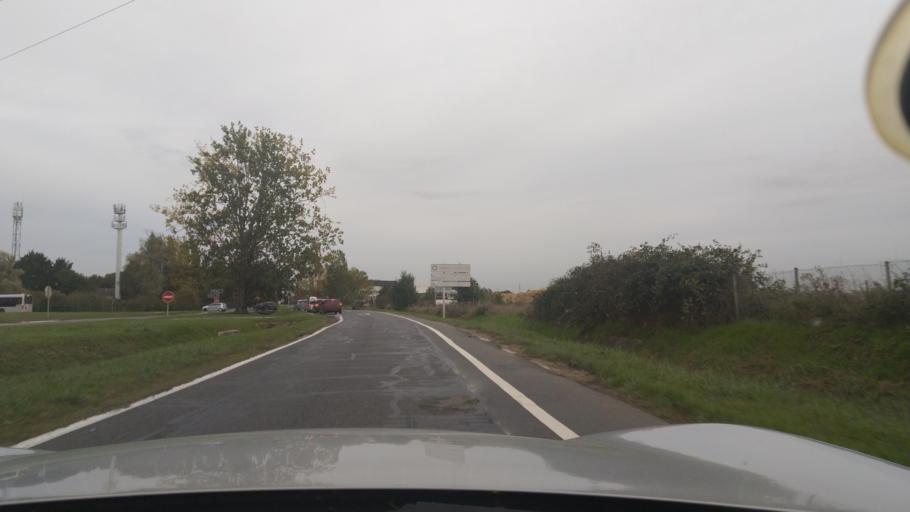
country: FR
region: Ile-de-France
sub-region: Departement de Seine-Saint-Denis
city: Villepinte
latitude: 48.9835
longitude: 2.5405
